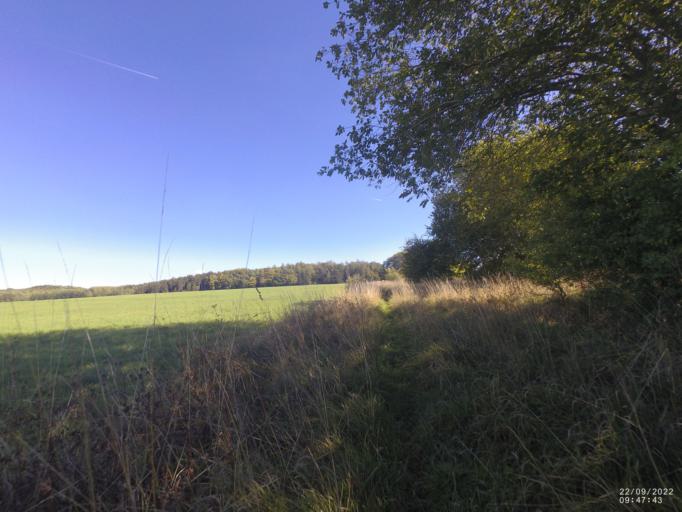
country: DE
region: Rheinland-Pfalz
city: Walsdorf
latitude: 50.2831
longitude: 6.7241
